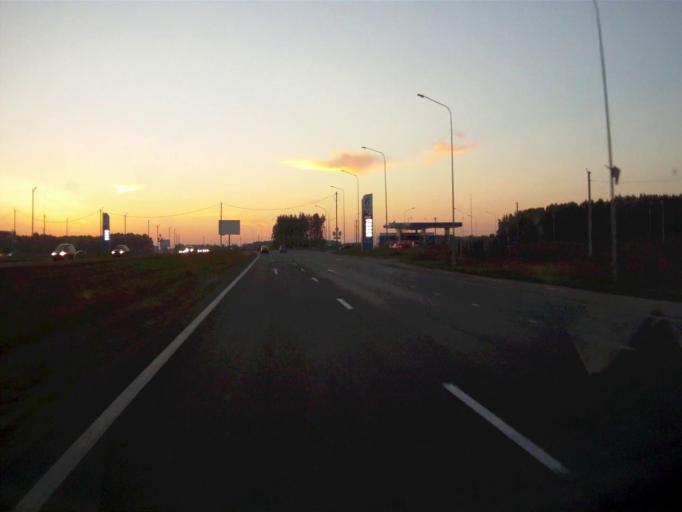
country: RU
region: Chelyabinsk
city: Roshchino
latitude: 55.1874
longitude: 61.2381
